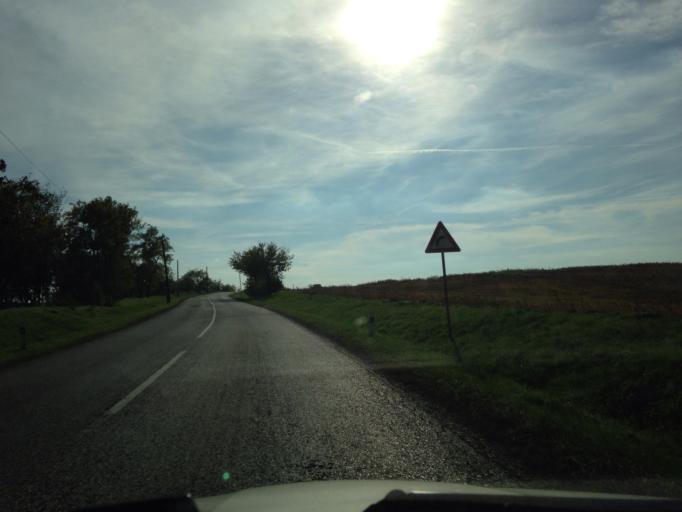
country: SK
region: Nitriansky
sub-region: Okres Komarno
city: Hurbanovo
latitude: 47.8730
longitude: 18.2832
